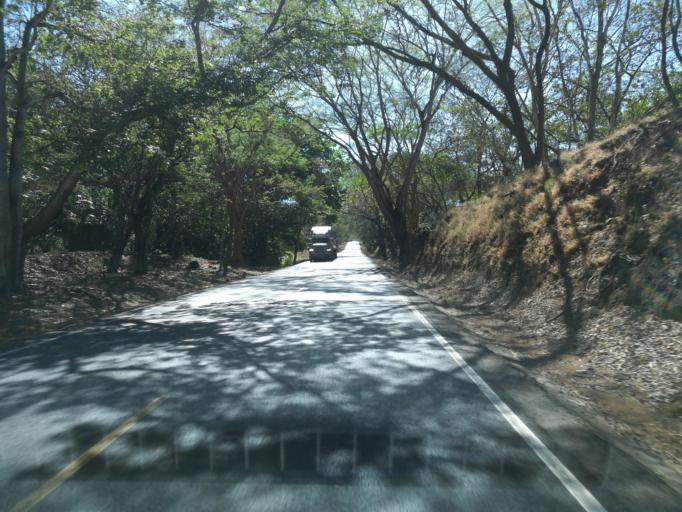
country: CR
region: Puntarenas
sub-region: Canton Central de Puntarenas
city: Puntarenas
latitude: 10.1094
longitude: -84.8865
